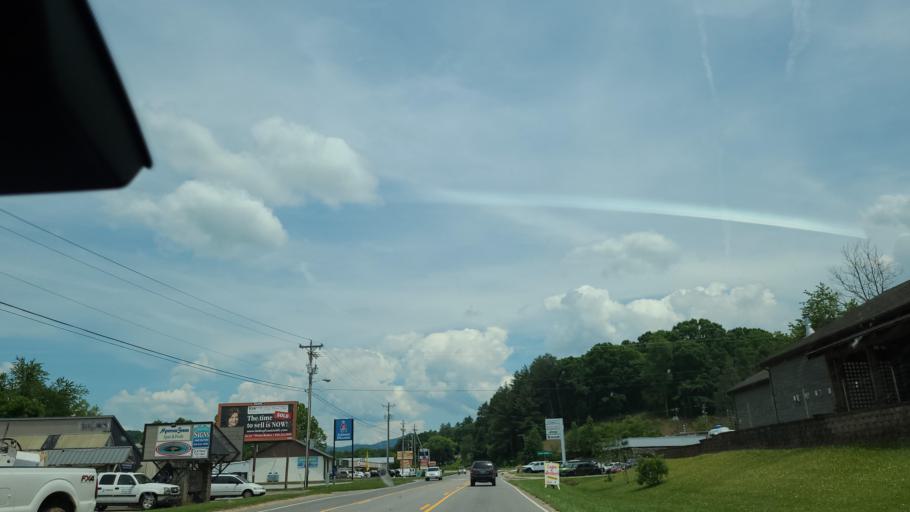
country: US
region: North Carolina
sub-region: Macon County
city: Franklin
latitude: 35.1786
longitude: -83.3673
